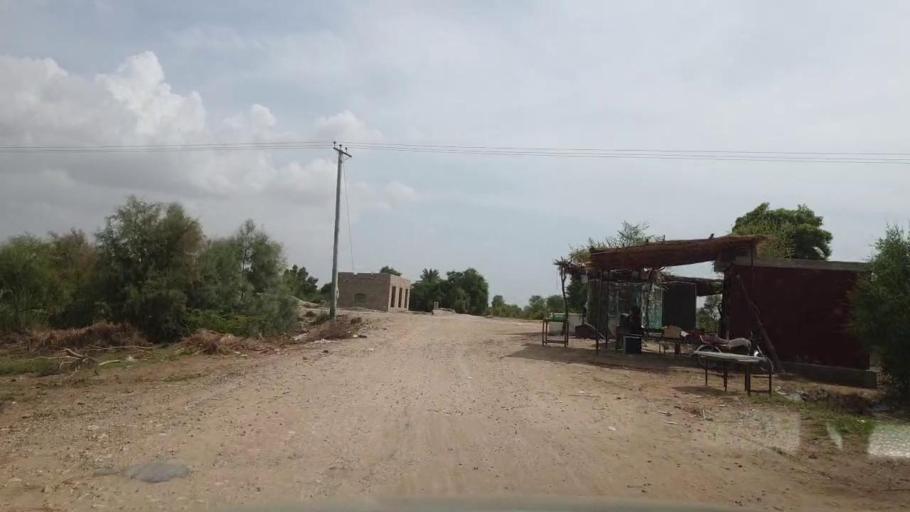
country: PK
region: Sindh
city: Kot Diji
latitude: 27.1107
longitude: 69.0223
